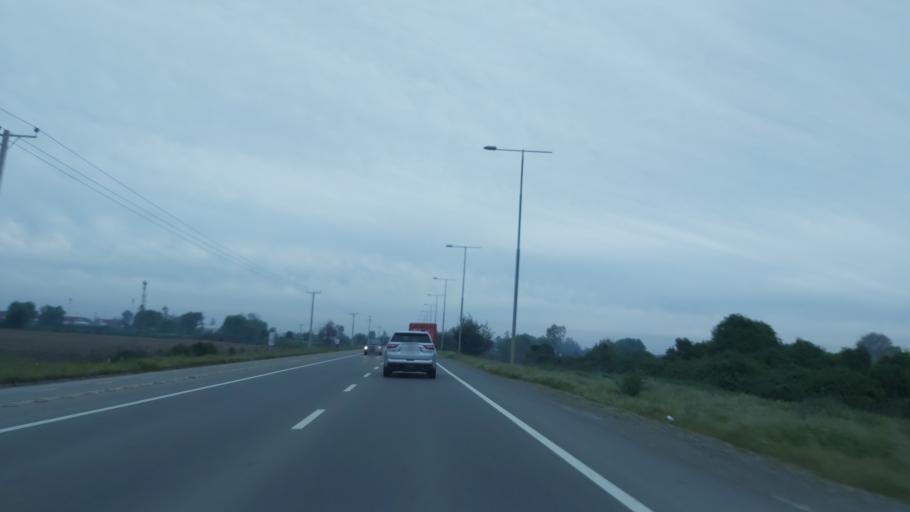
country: CL
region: Maule
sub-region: Provincia de Linares
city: Linares
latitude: -35.8280
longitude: -71.6069
